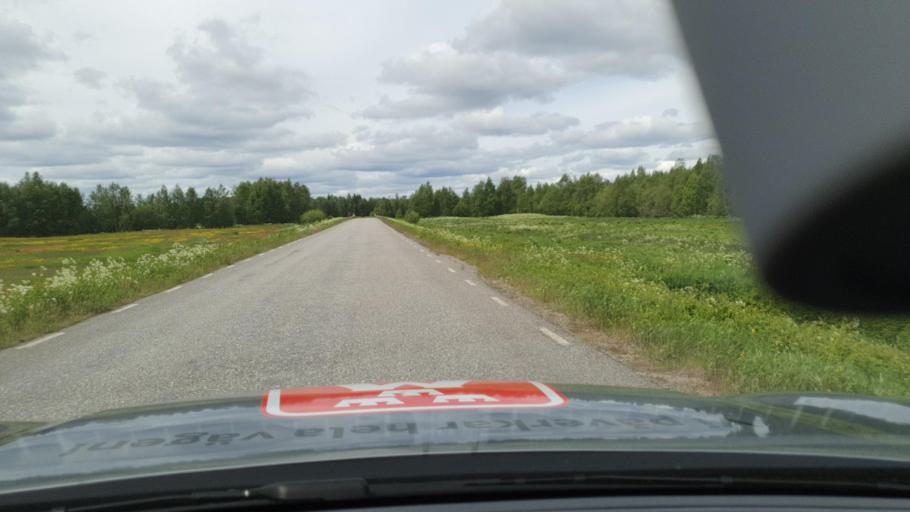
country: FI
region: Lapland
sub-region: Torniolaakso
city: Ylitornio
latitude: 66.0411
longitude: 23.7267
